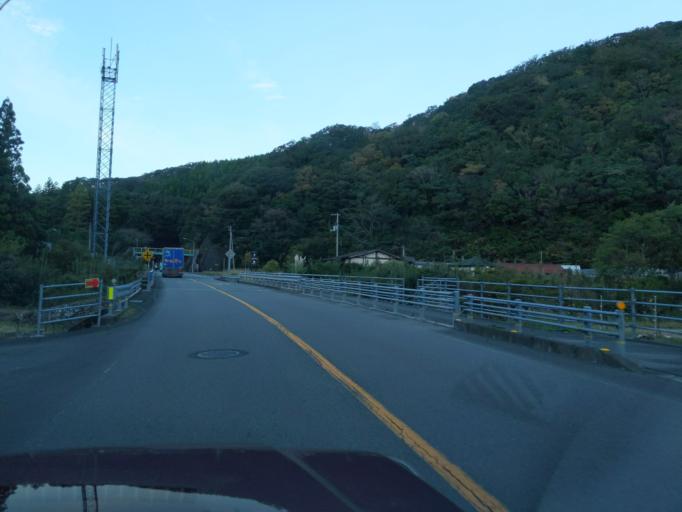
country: JP
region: Tokushima
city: Anan
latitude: 33.7174
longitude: 134.4864
